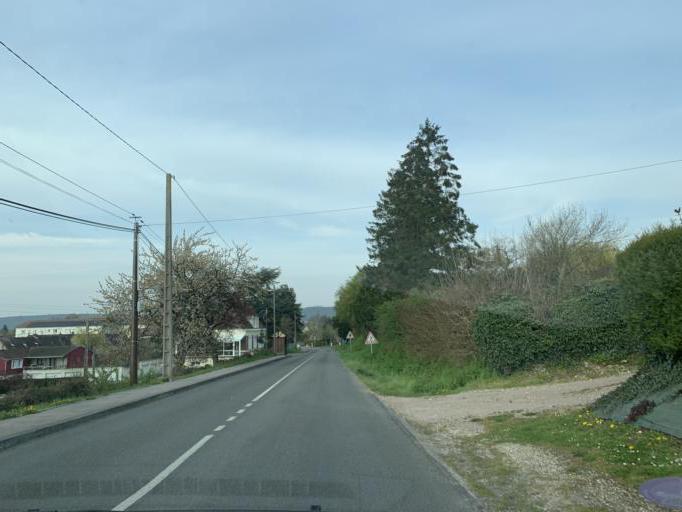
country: FR
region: Haute-Normandie
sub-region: Departement de la Seine-Maritime
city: La Mailleraye-sur-Seine
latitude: 49.4764
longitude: 0.7735
